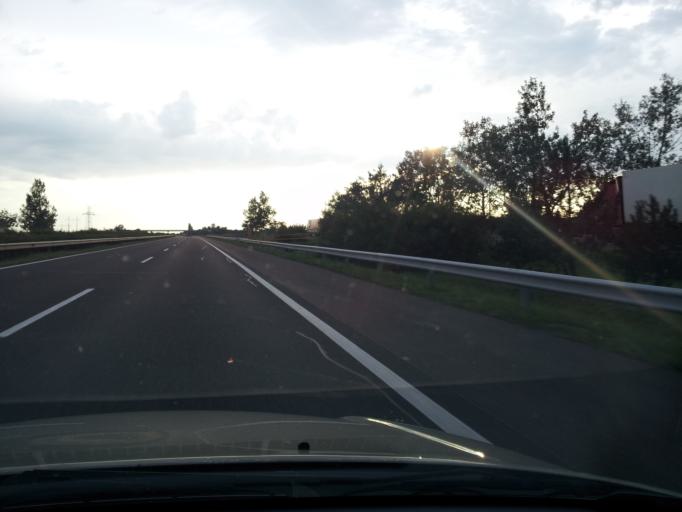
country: HU
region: Heves
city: Kompolt
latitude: 47.7067
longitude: 20.1421
